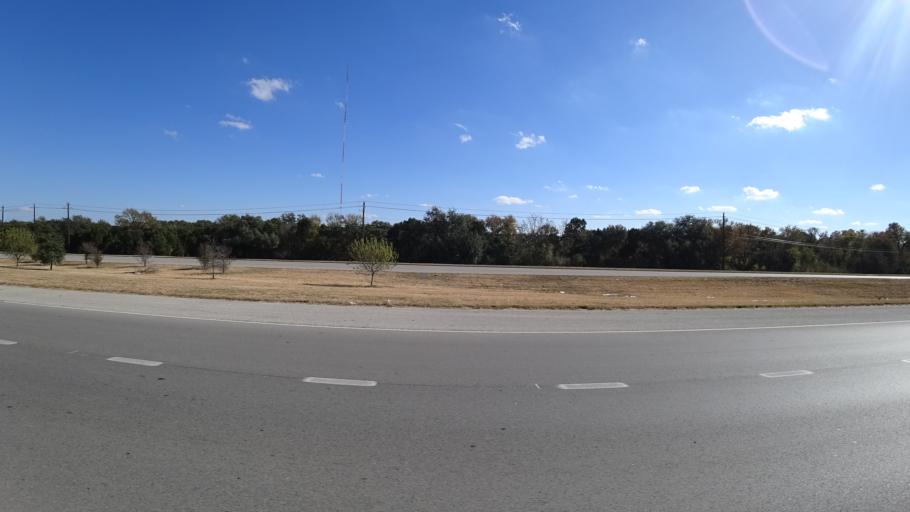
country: US
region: Texas
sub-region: Travis County
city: Rollingwood
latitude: 30.2251
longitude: -97.8323
